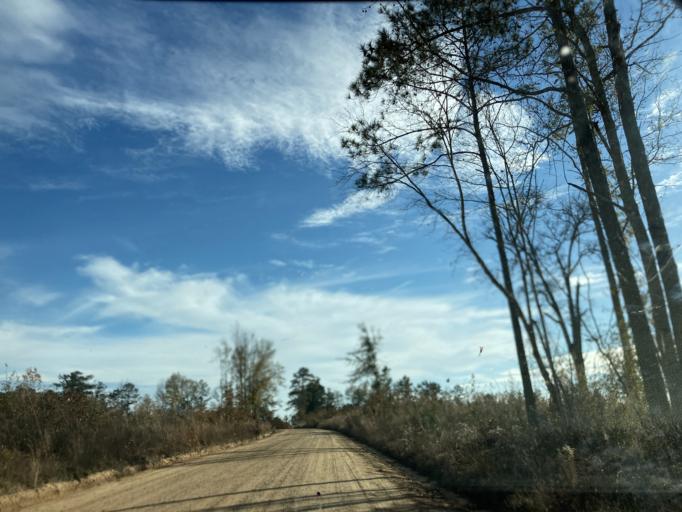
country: US
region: Georgia
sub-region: Jones County
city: Gray
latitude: 32.8934
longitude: -83.4888
